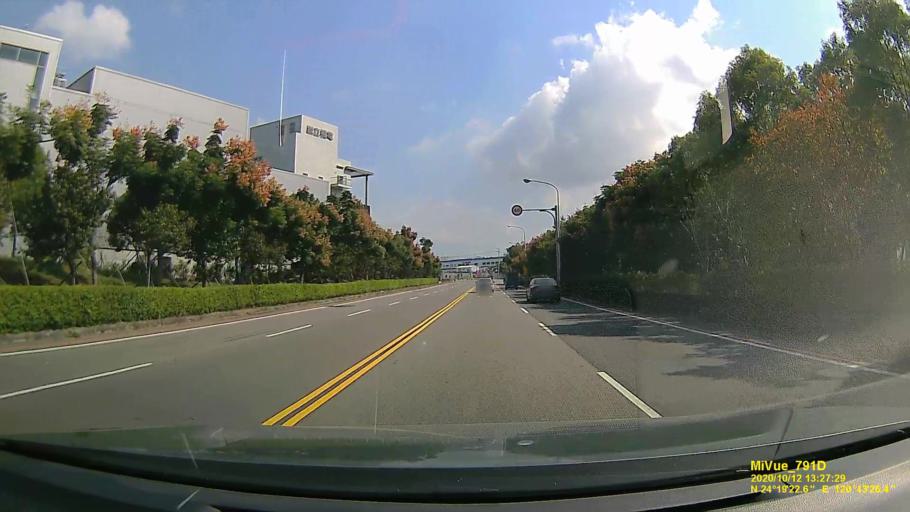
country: TW
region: Taiwan
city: Fengyuan
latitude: 24.3226
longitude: 120.7244
